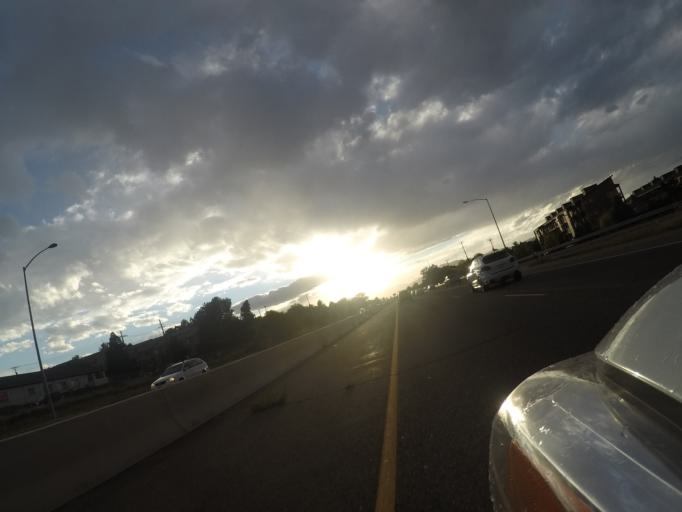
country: US
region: Colorado
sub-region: Arapahoe County
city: Sheridan
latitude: 39.6533
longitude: -105.0561
